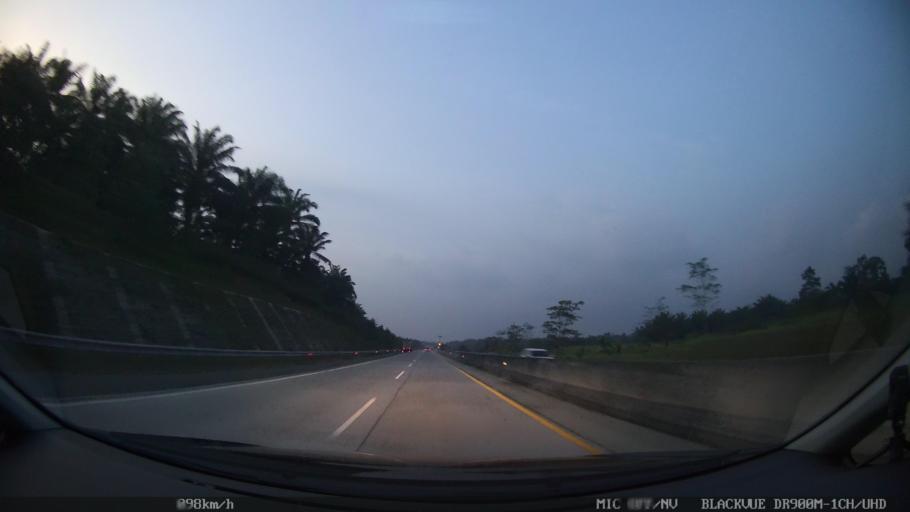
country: ID
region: Lampung
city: Sidorejo
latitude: -5.5507
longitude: 105.5246
